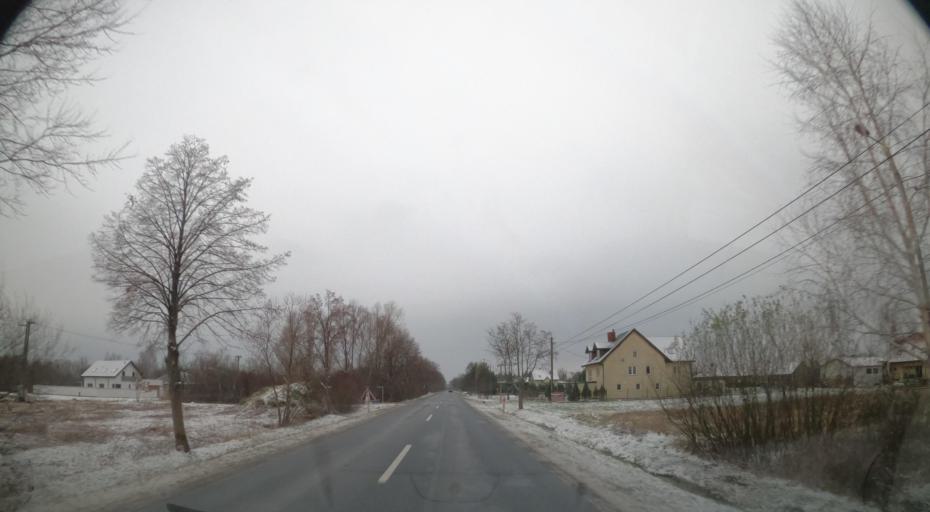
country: PL
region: Masovian Voivodeship
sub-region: Powiat plocki
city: Maszewo Duze
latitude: 52.5715
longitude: 19.6012
